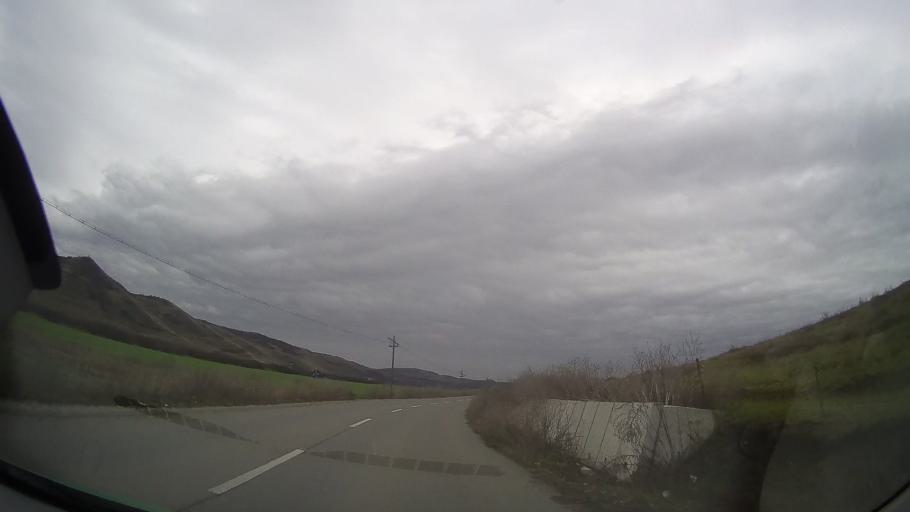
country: RO
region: Mures
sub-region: Comuna Craesti
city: Craiesti
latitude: 46.7820
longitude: 24.4268
